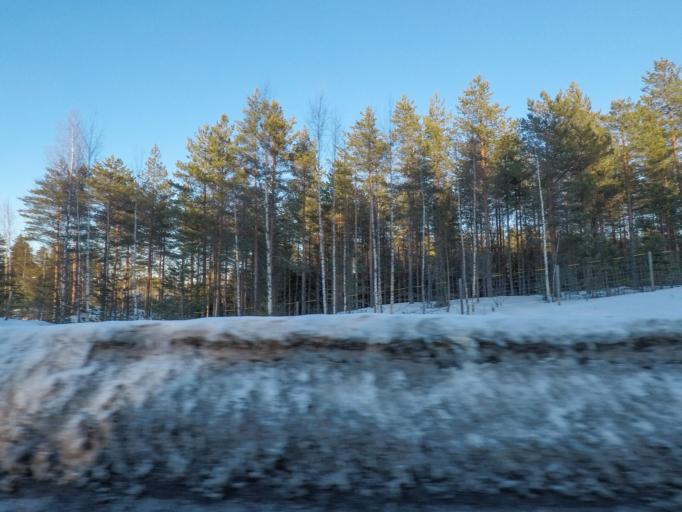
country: FI
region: Southern Savonia
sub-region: Mikkeli
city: Pertunmaa
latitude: 61.4186
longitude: 26.4347
